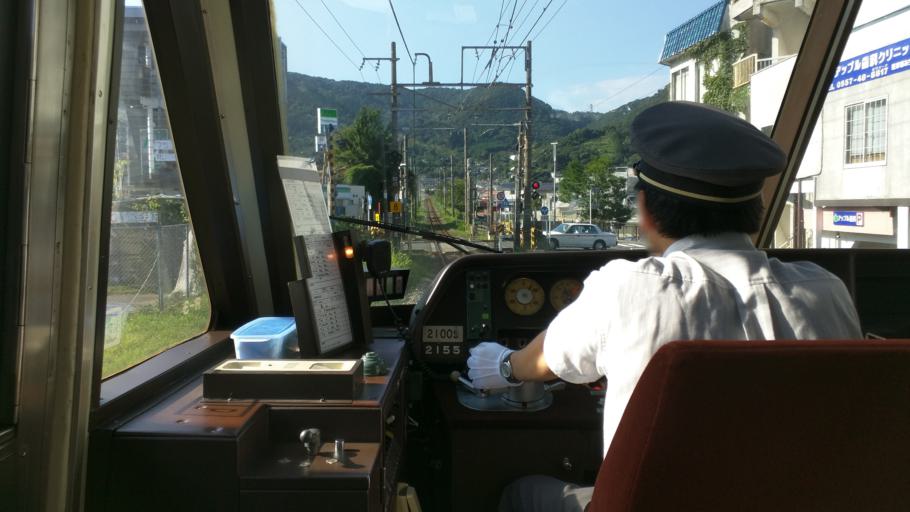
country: JP
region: Shizuoka
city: Ito
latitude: 35.0072
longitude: 139.0793
